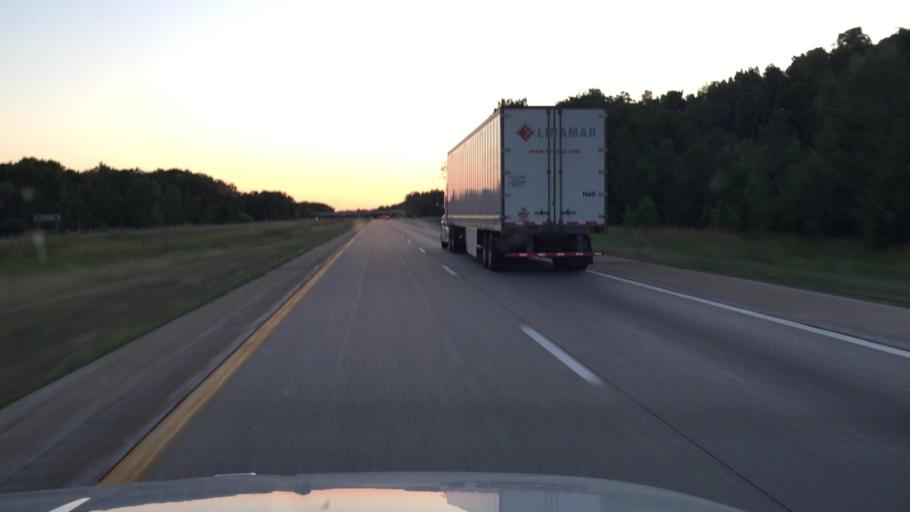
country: US
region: Michigan
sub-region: Shiawassee County
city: Perry
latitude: 42.8410
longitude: -84.2089
